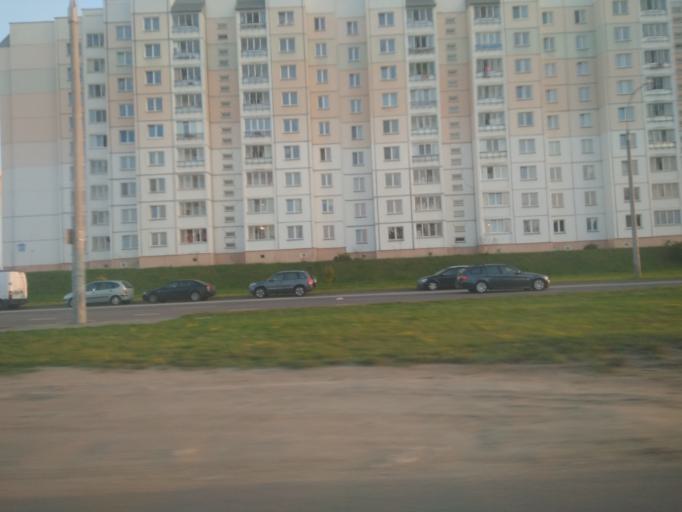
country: BY
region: Minsk
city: Novoye Medvezhino
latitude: 53.9209
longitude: 27.4629
